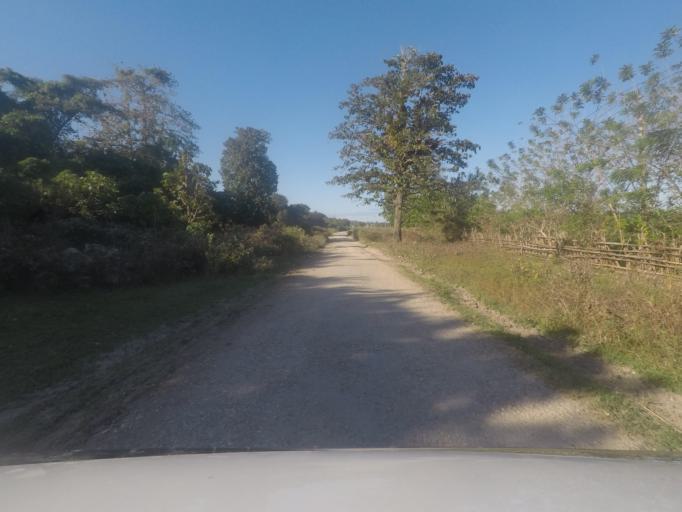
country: TL
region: Lautem
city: Lospalos
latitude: -8.4075
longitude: 127.1718
